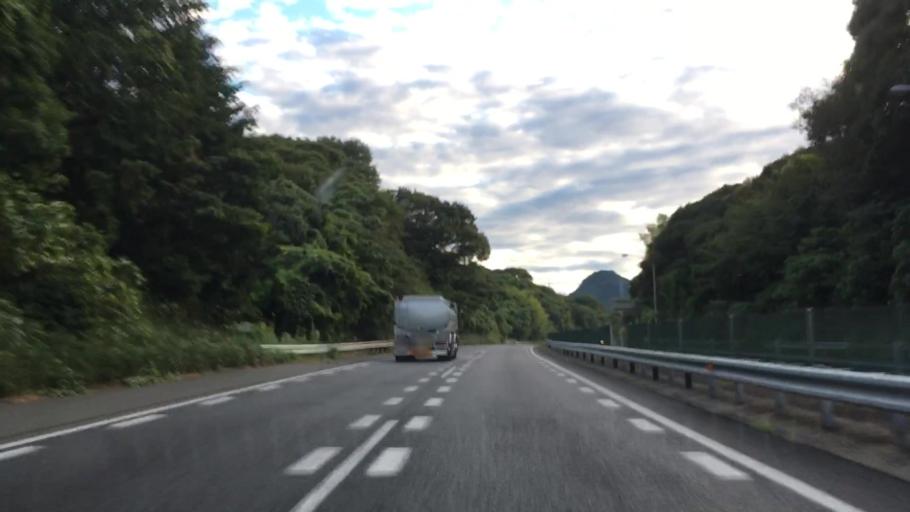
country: JP
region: Yamaguchi
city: Shimonoseki
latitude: 34.0477
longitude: 131.0014
